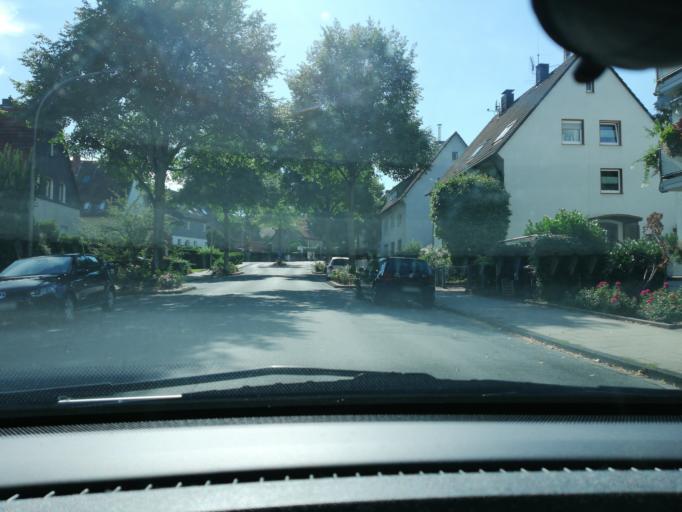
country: DE
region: North Rhine-Westphalia
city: Witten
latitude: 51.4494
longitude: 7.3948
